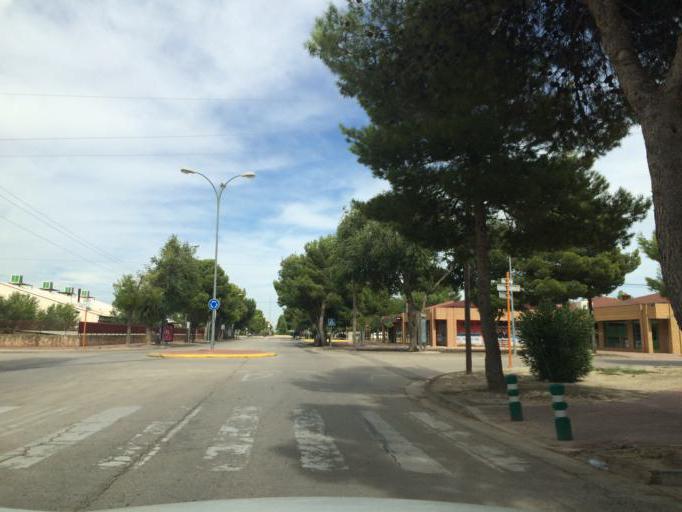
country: ES
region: Castille-La Mancha
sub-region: Provincia de Albacete
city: Albacete
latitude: 39.0131
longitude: -1.8807
